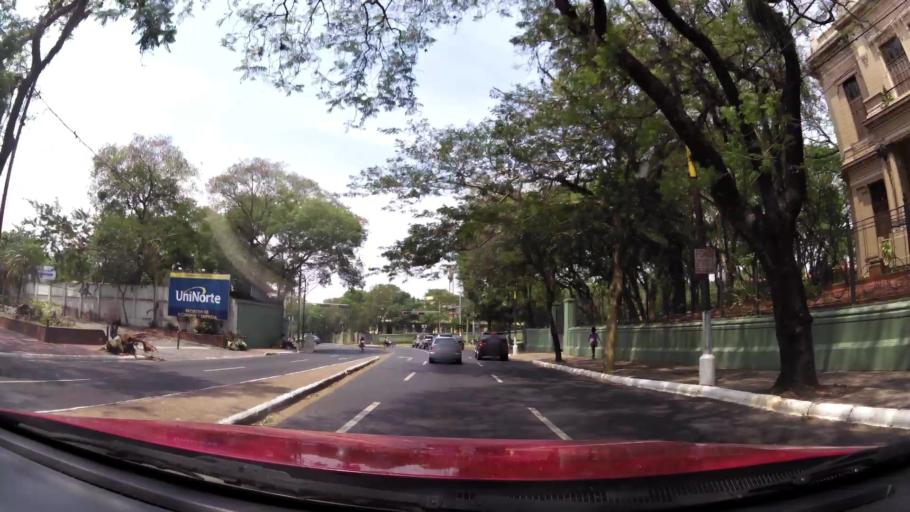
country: PY
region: Asuncion
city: Asuncion
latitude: -25.2936
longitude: -57.6119
